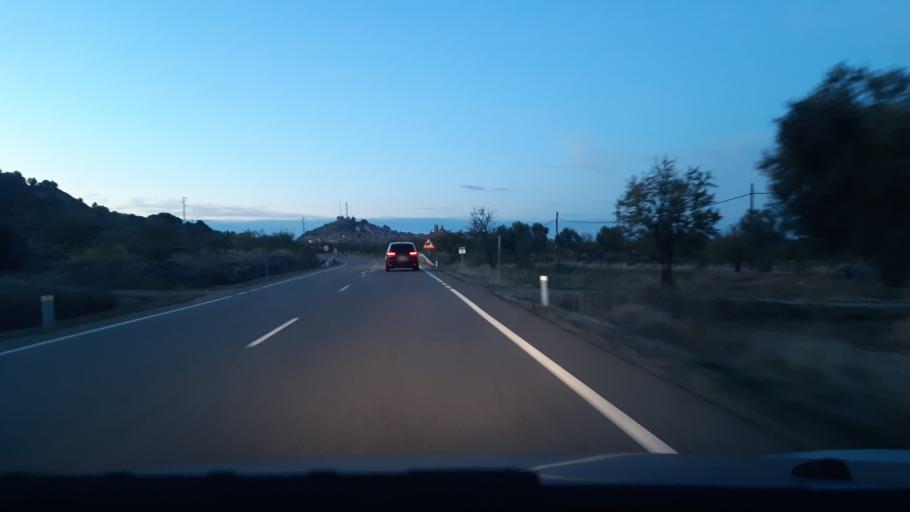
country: ES
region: Aragon
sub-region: Provincia de Teruel
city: Calaceite
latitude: 41.0062
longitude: 0.1920
